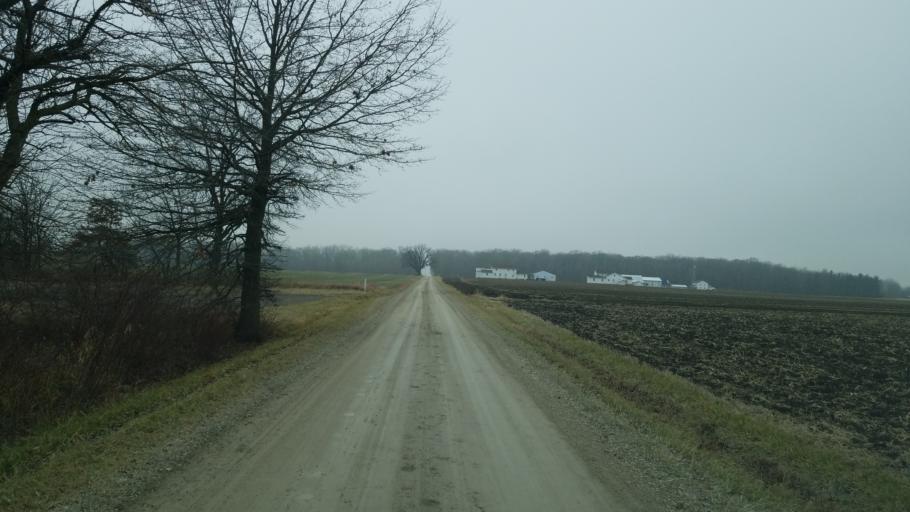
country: US
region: Indiana
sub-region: Adams County
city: Geneva
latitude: 40.5839
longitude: -85.0011
